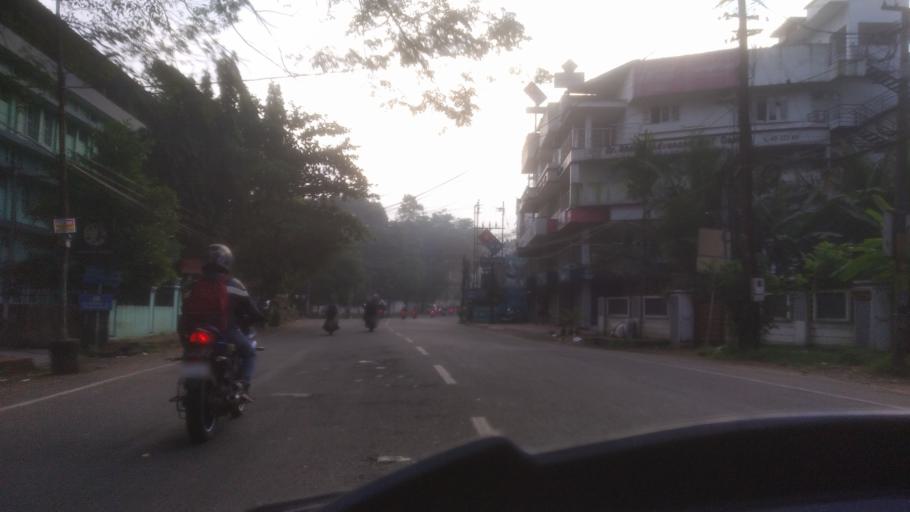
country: IN
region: Kerala
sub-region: Ernakulam
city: Aluva
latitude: 10.1128
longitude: 76.3561
